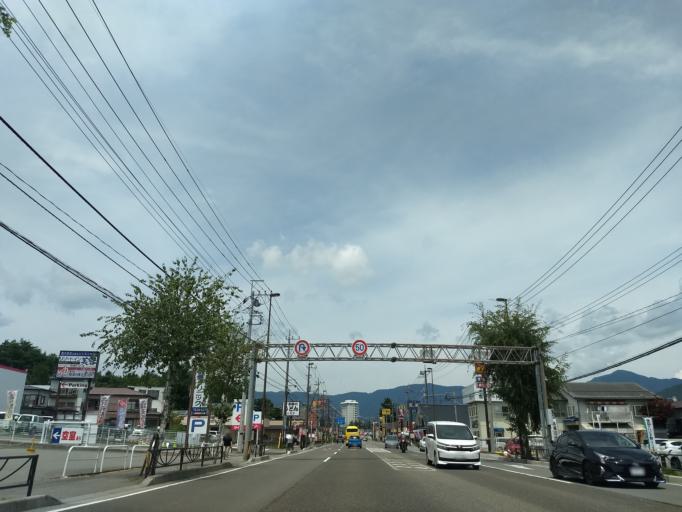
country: JP
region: Yamanashi
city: Fujikawaguchiko
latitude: 35.4791
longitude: 138.7856
